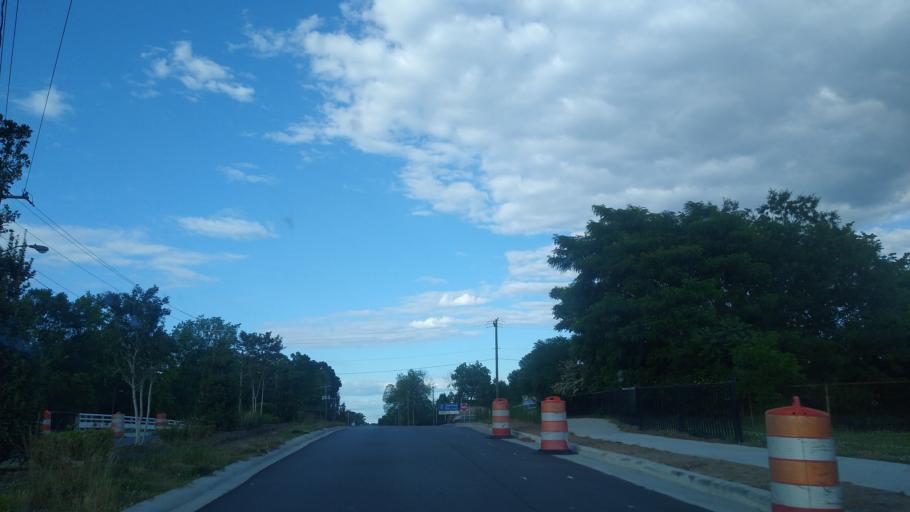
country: US
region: North Carolina
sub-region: Guilford County
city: Greensboro
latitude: 36.0783
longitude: -79.7842
